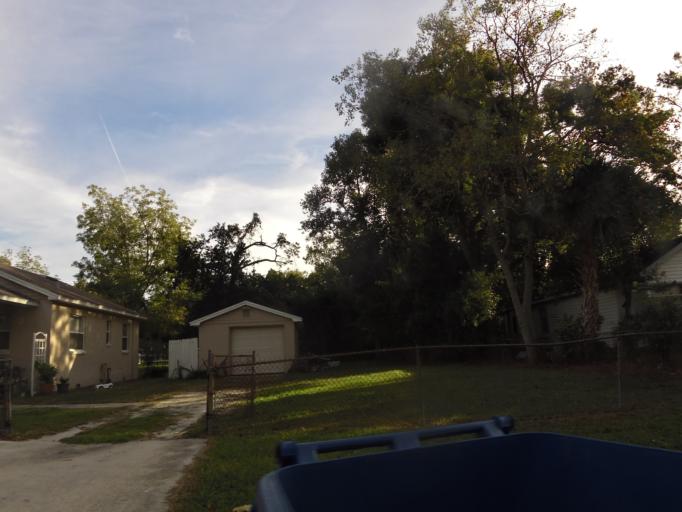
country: US
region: Florida
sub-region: Duval County
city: Jacksonville
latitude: 30.4113
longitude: -81.6524
